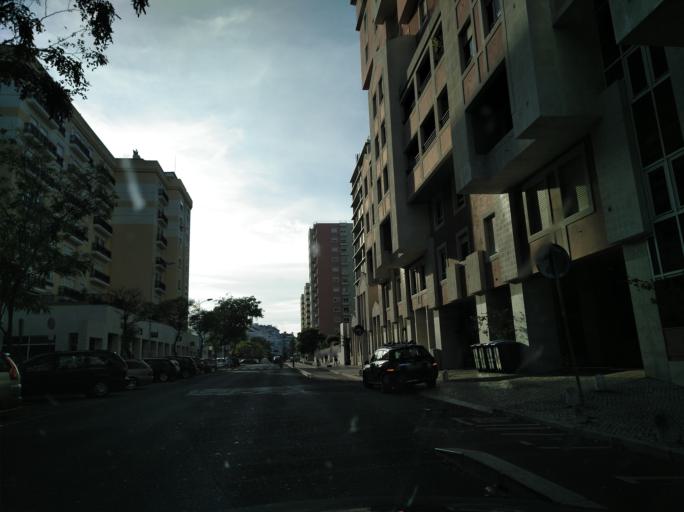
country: PT
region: Lisbon
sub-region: Odivelas
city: Pontinha
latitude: 38.7601
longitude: -9.1763
